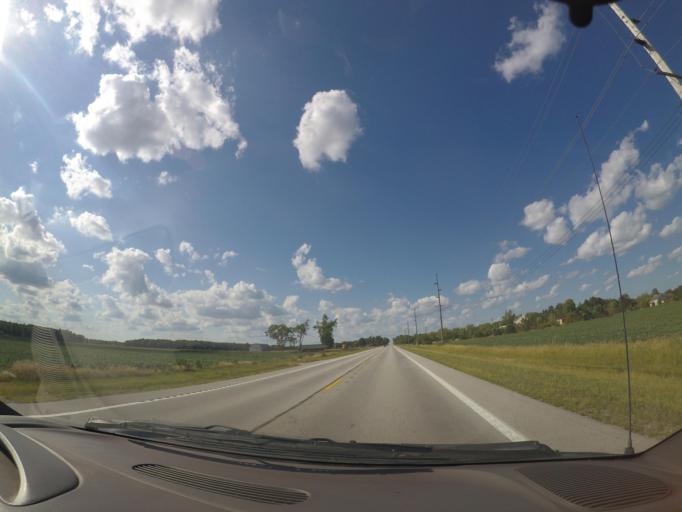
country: US
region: Ohio
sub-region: Wood County
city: Pemberville
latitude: 41.4044
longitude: -83.4160
